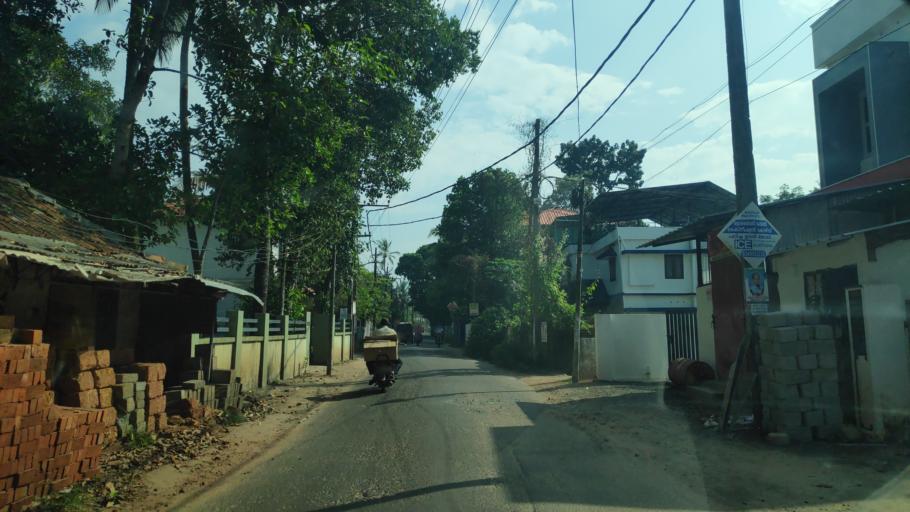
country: IN
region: Kerala
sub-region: Alappuzha
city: Alleppey
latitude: 9.5064
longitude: 76.3205
